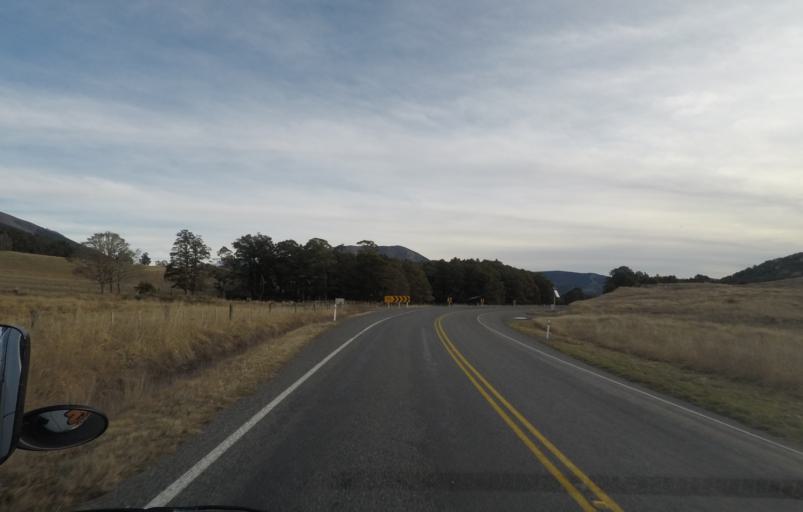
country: NZ
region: Tasman
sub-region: Tasman District
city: Wakefield
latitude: -41.7992
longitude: 172.8681
